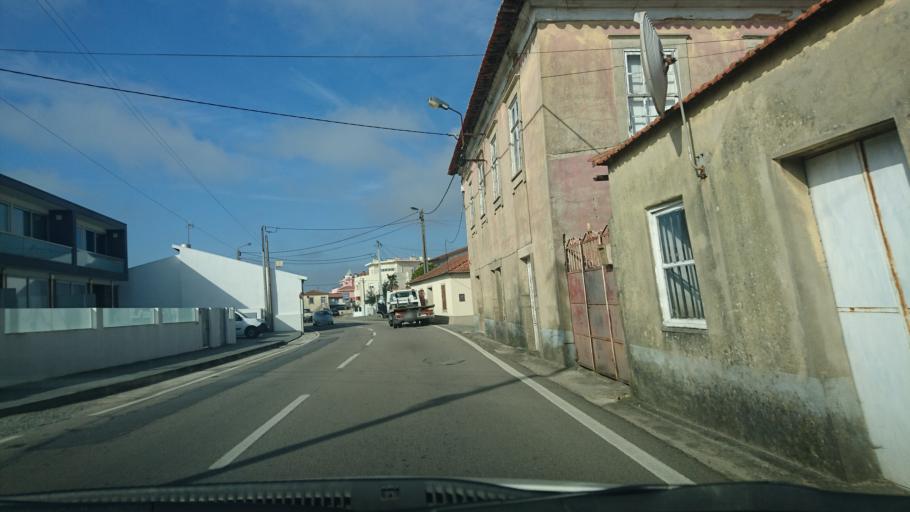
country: PT
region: Aveiro
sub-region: Ovar
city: Esmoriz
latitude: 40.9718
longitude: -8.6297
